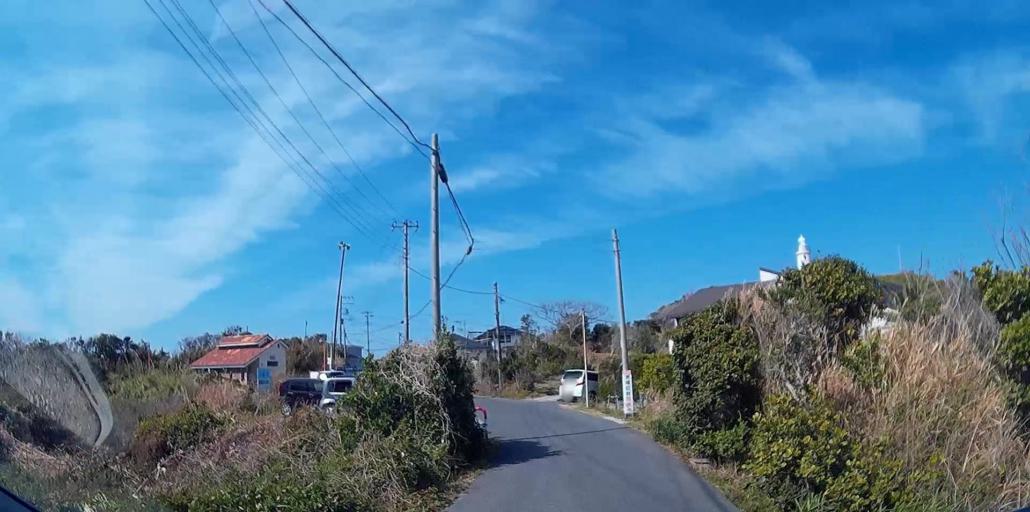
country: JP
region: Chiba
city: Tateyama
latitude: 34.9740
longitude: 139.7582
